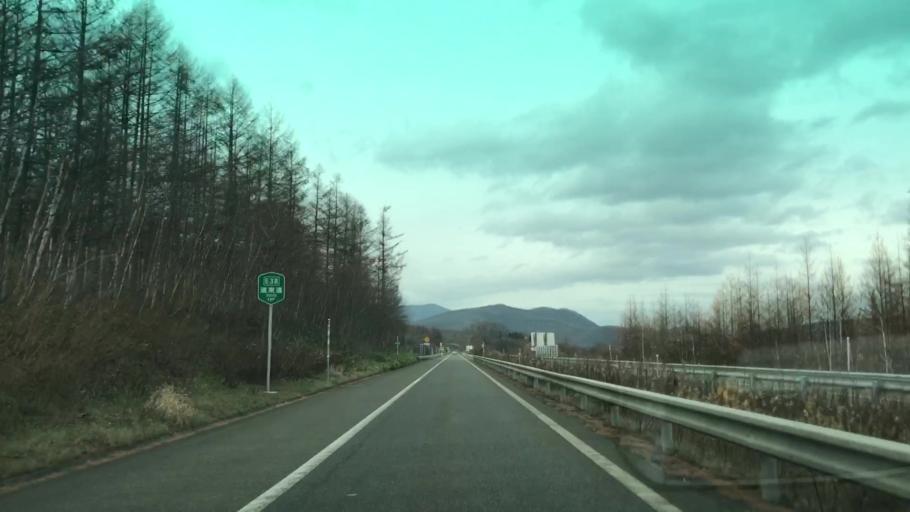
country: JP
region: Hokkaido
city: Otofuke
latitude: 42.9990
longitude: 142.8514
